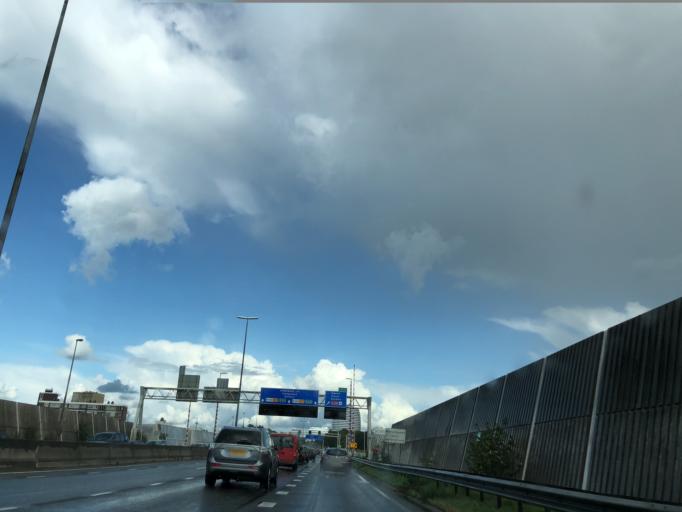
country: NL
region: Groningen
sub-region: Gemeente Groningen
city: Groningen
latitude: 53.2021
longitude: 6.5606
